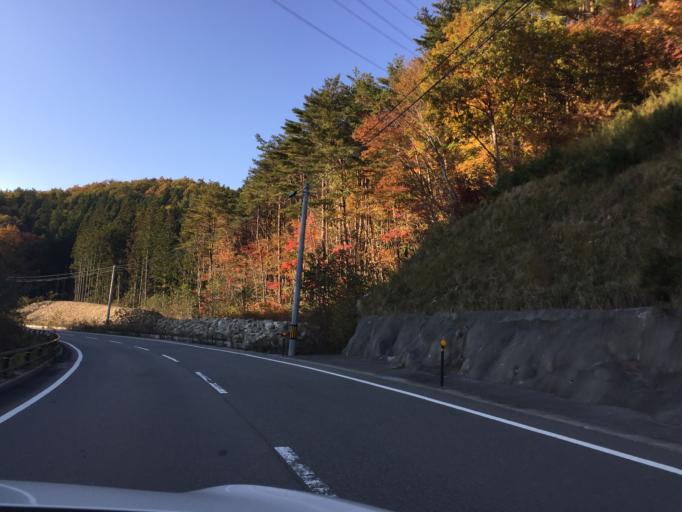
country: JP
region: Fukushima
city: Funehikimachi-funehiki
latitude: 37.2912
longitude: 140.7512
